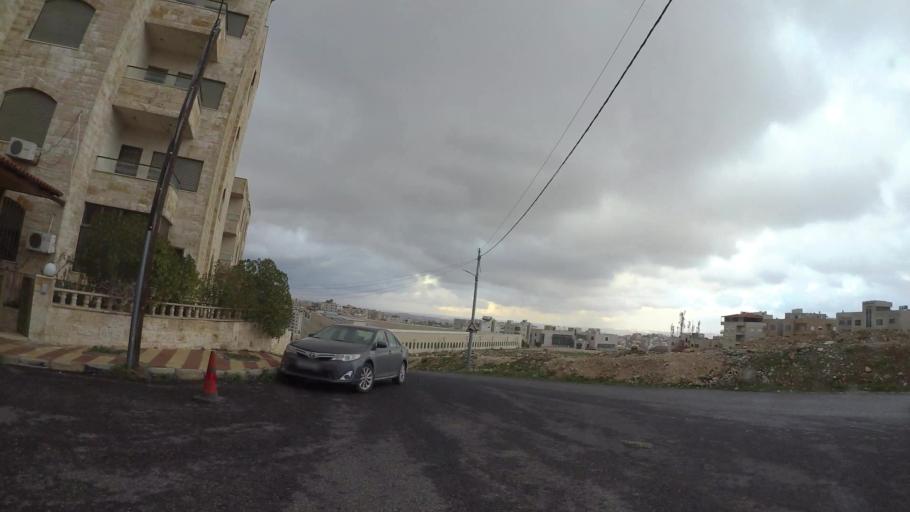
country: JO
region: Amman
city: Amman
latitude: 32.0071
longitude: 35.9303
